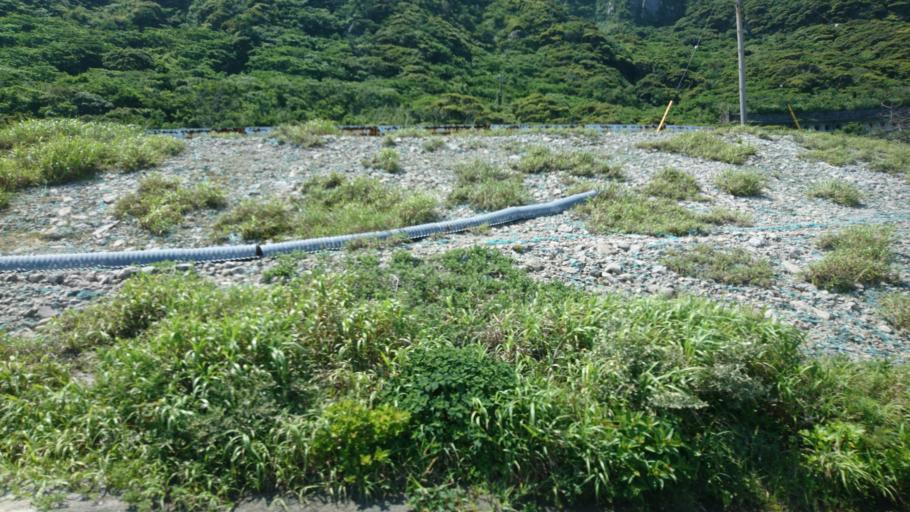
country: JP
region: Shizuoka
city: Shimoda
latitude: 34.3922
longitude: 139.2778
